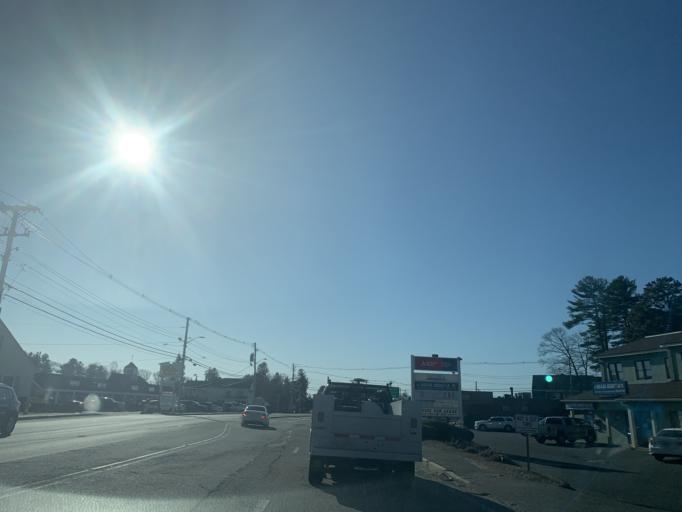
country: US
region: Massachusetts
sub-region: Middlesex County
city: Marlborough
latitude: 42.3488
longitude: -71.5070
